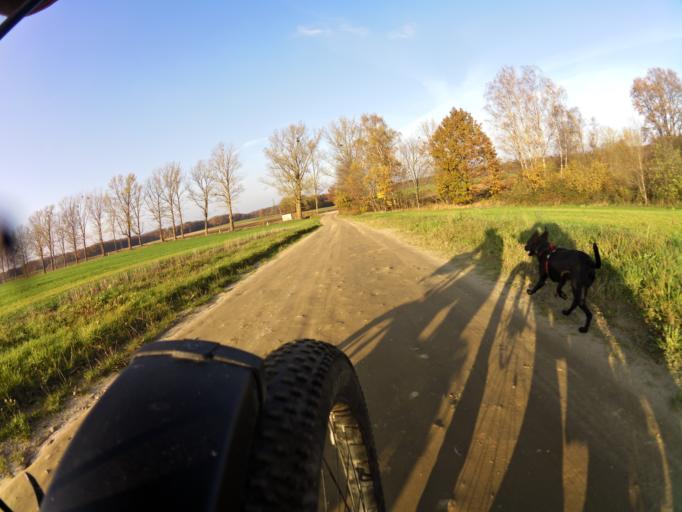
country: PL
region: Pomeranian Voivodeship
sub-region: Powiat pucki
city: Krokowa
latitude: 54.7347
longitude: 18.1965
